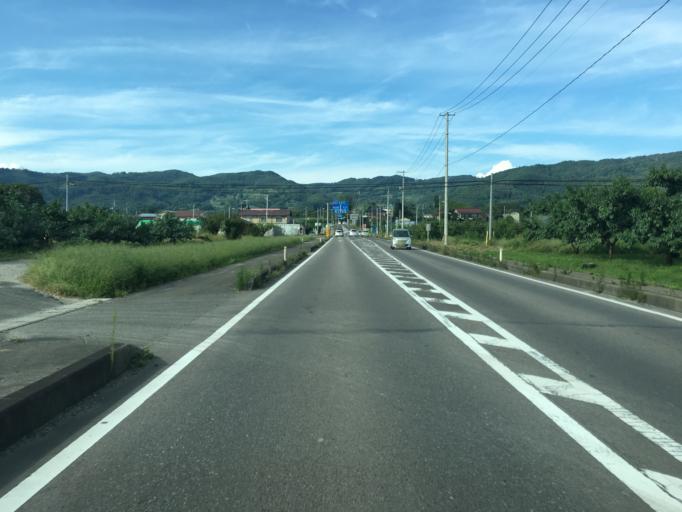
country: JP
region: Fukushima
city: Fukushima-shi
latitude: 37.8253
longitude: 140.4661
